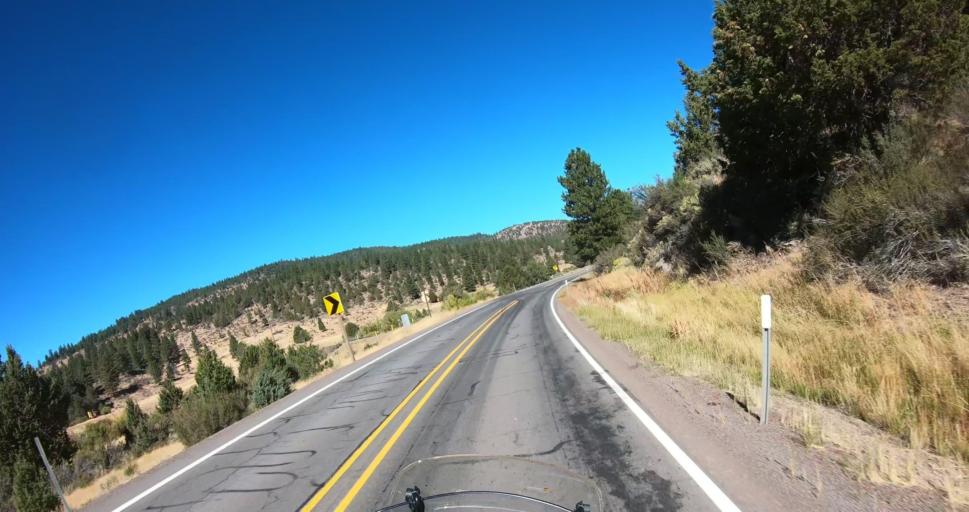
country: US
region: Oregon
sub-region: Lake County
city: Lakeview
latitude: 42.3850
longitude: -120.3063
